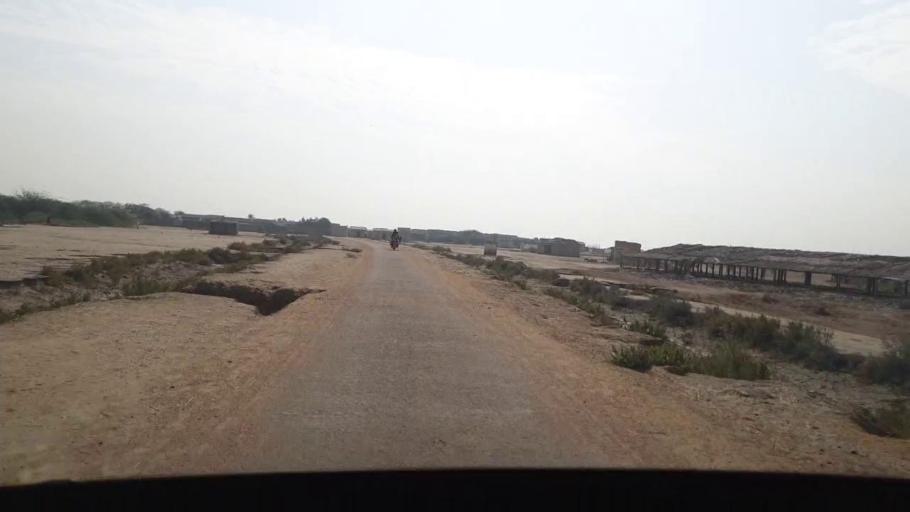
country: PK
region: Sindh
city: Chuhar Jamali
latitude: 24.2377
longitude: 67.9845
